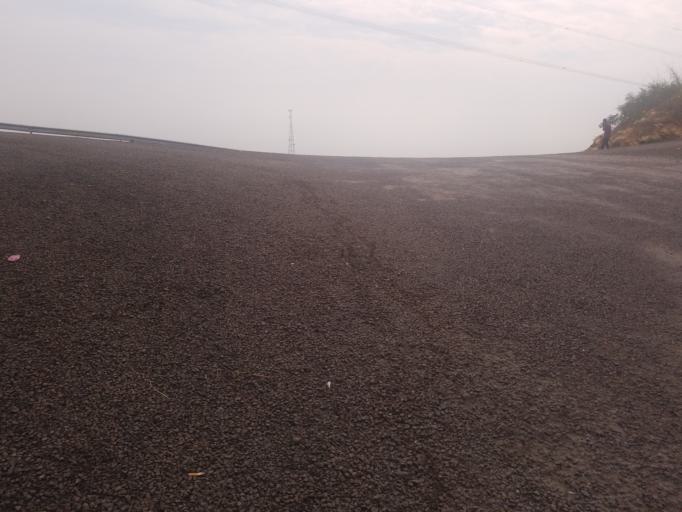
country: GH
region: Western
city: Tarkwa
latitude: 5.3009
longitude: -1.9958
